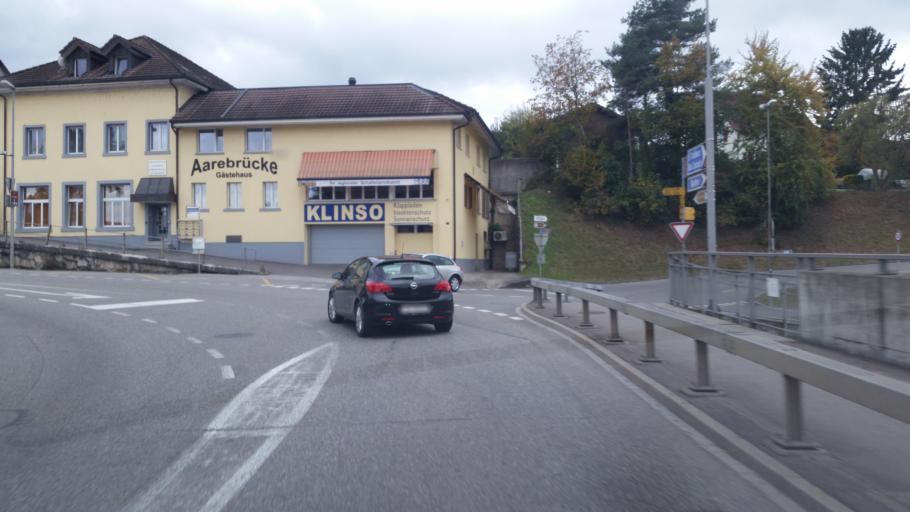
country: CH
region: Aargau
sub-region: Bezirk Brugg
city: Lauffohr (Brugg)
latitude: 47.5147
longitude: 8.2323
